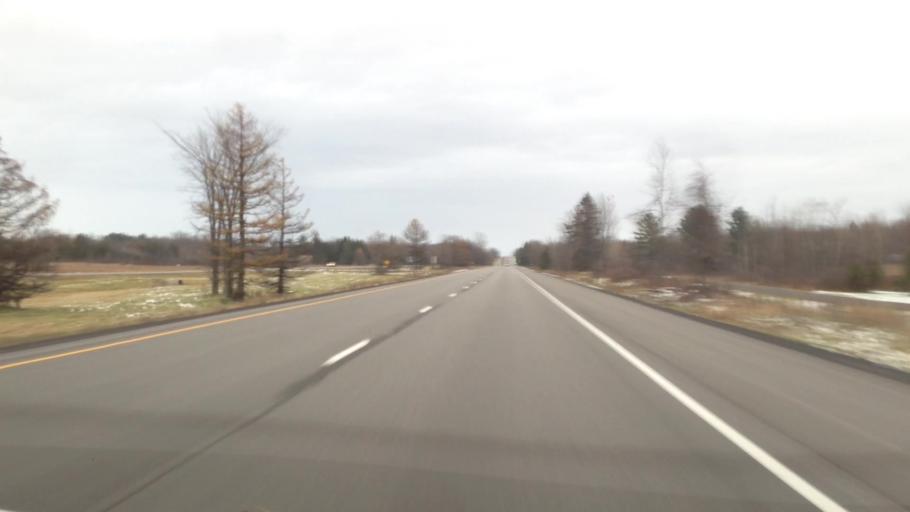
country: CA
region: Quebec
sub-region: Monteregie
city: Rigaud
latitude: 45.5456
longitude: -74.4166
